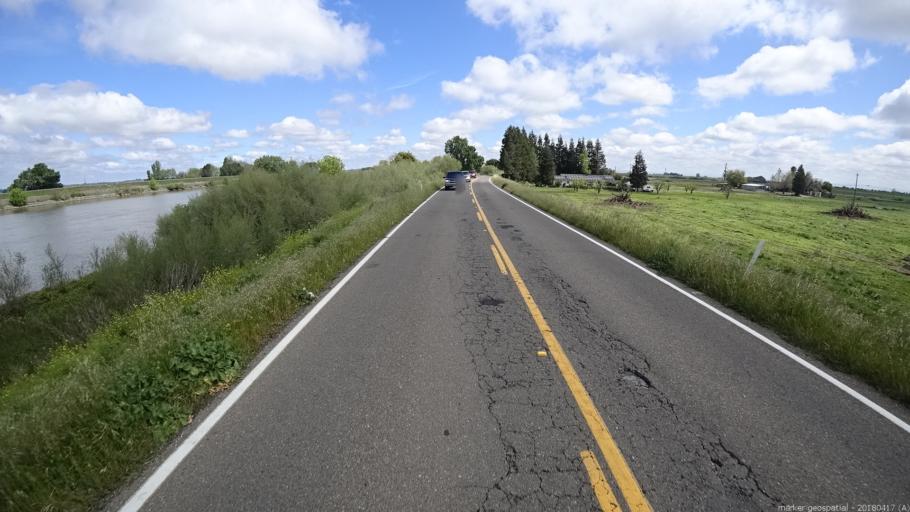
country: US
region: California
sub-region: Sacramento County
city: Walnut Grove
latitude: 38.1854
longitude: -121.5820
